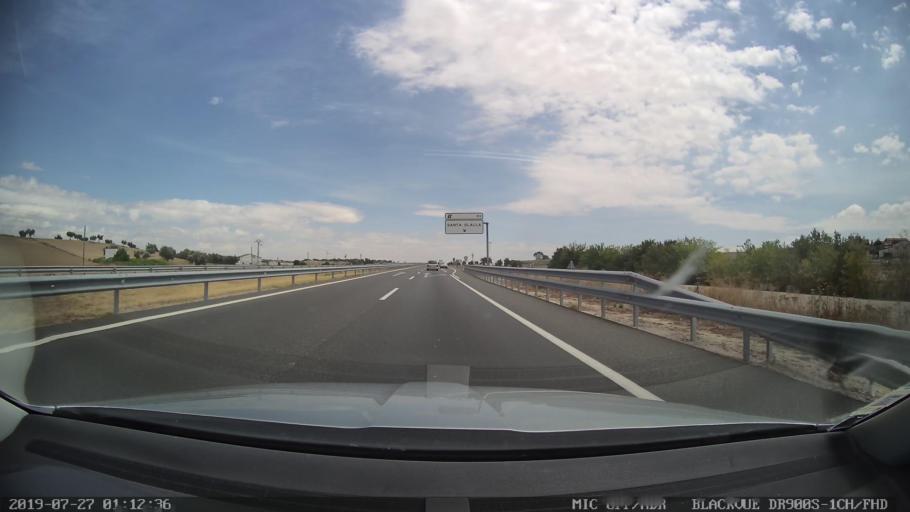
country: ES
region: Castille-La Mancha
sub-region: Province of Toledo
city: Santa Olalla
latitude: 40.0259
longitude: -4.4600
